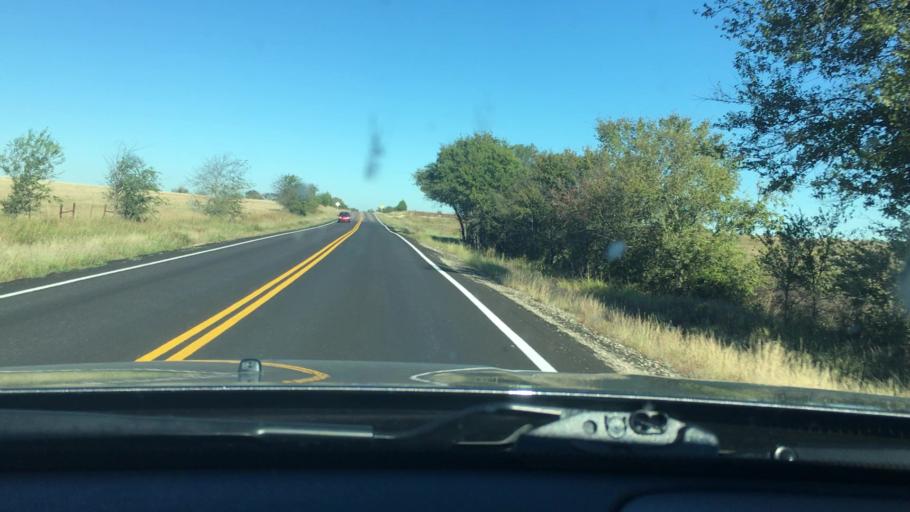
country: US
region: Oklahoma
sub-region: Johnston County
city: Tishomingo
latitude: 34.1651
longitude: -96.7079
